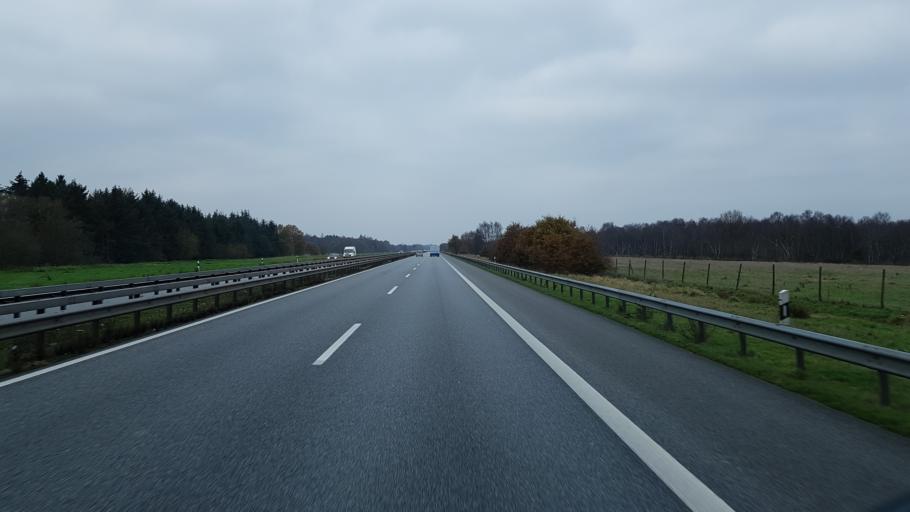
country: DE
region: Lower Saxony
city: Uthlede
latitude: 53.3448
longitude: 8.6029
